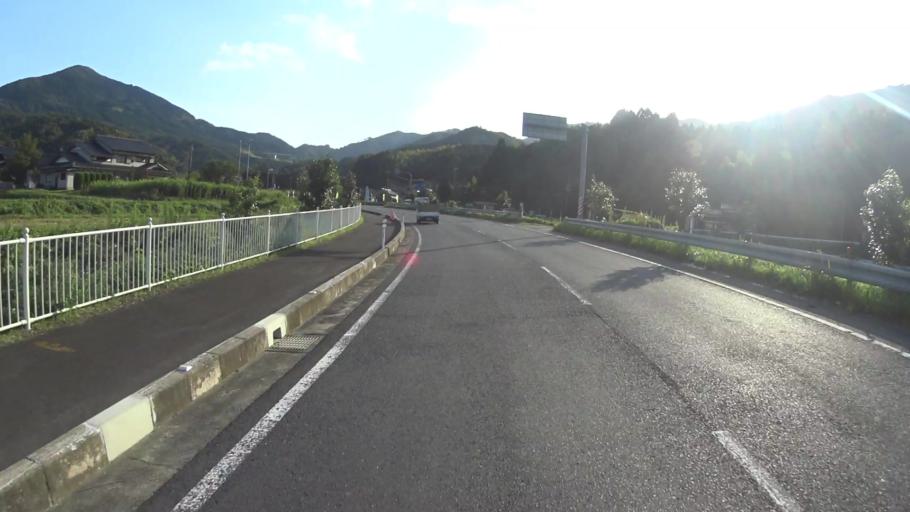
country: JP
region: Kyoto
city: Miyazu
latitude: 35.4697
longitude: 135.0855
